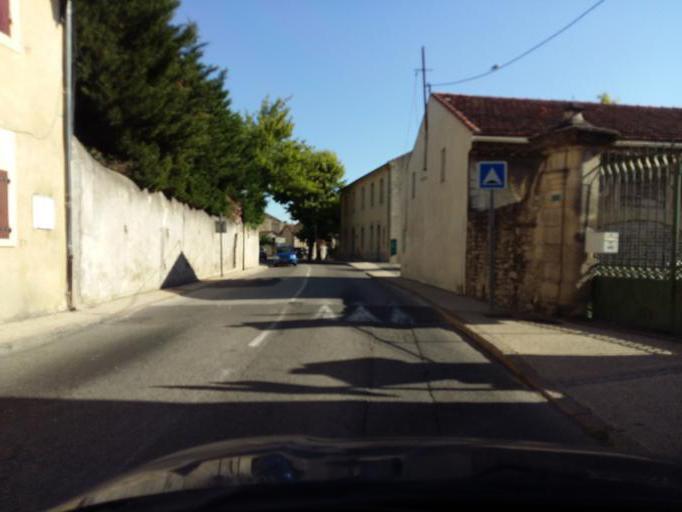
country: FR
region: Provence-Alpes-Cote d'Azur
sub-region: Departement du Vaucluse
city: Visan
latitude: 44.3151
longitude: 4.9490
